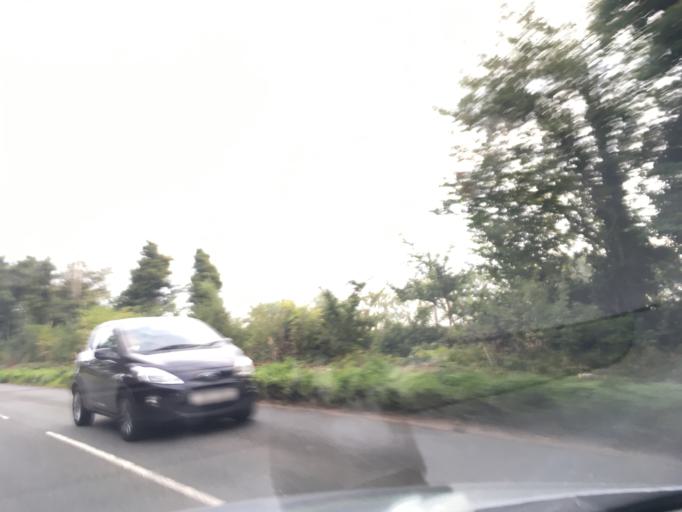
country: GB
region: England
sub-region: Oxfordshire
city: Cowley
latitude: 51.7713
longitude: -1.1902
